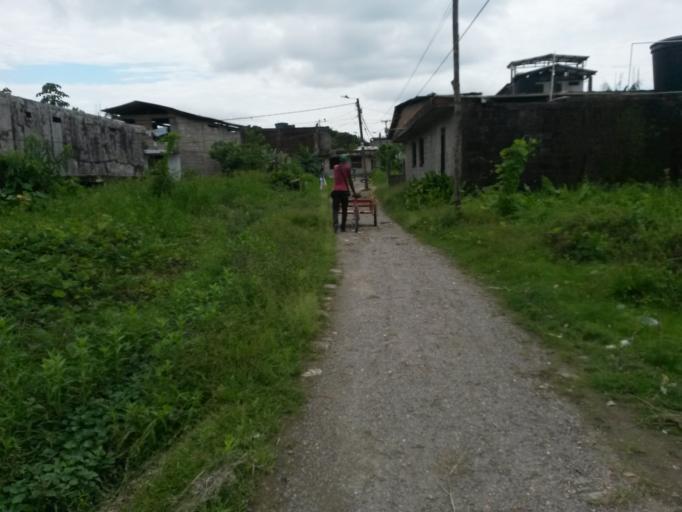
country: CO
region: Cauca
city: Guapi
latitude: 2.5701
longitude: -77.8898
